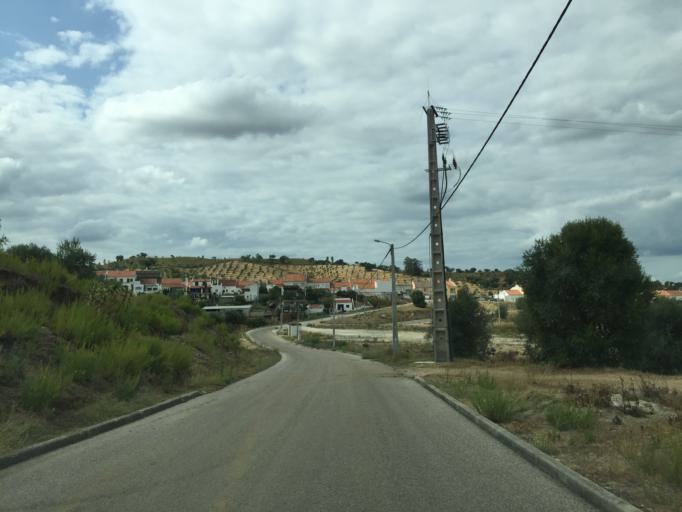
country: PT
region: Portalegre
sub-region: Ponte de Sor
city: Santo Andre
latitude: 39.0793
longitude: -8.1729
